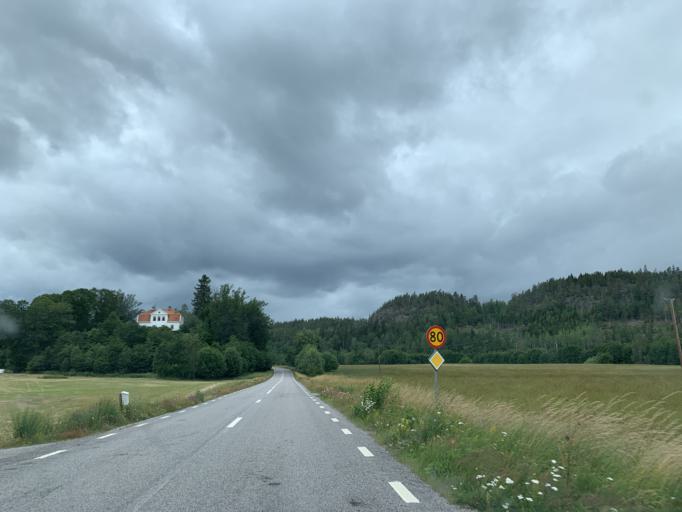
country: SE
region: Kalmar
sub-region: Vasterviks Kommun
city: Overum
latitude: 58.0153
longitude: 16.1672
